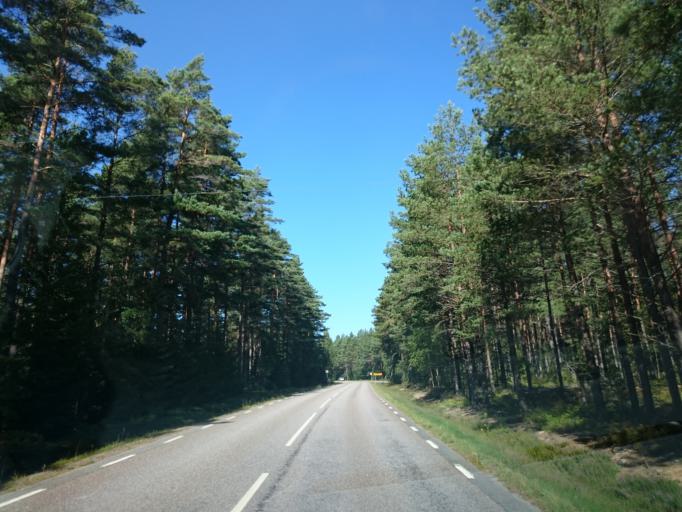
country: SE
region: OEstergoetland
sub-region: Norrkopings Kommun
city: Krokek
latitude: 58.6546
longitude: 16.5347
